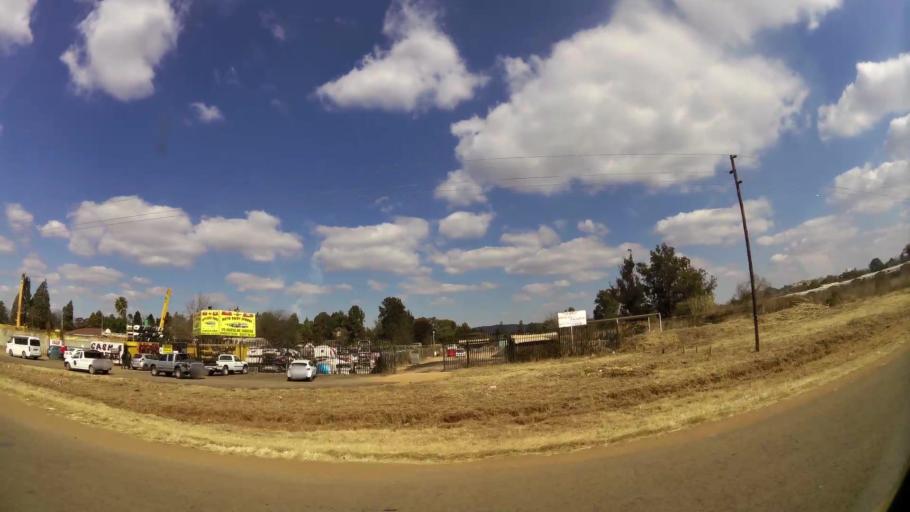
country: ZA
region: Gauteng
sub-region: City of Tshwane Metropolitan Municipality
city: Pretoria
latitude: -25.7417
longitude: 28.3409
